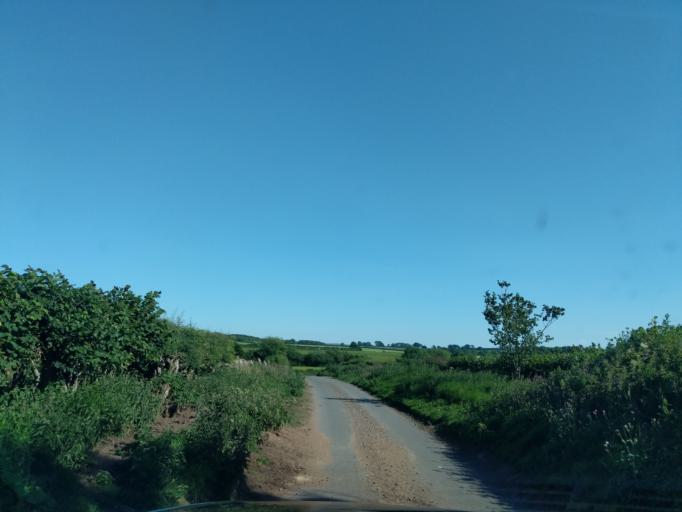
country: GB
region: Scotland
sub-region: East Lothian
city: Ormiston
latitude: 55.8813
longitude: -2.9346
